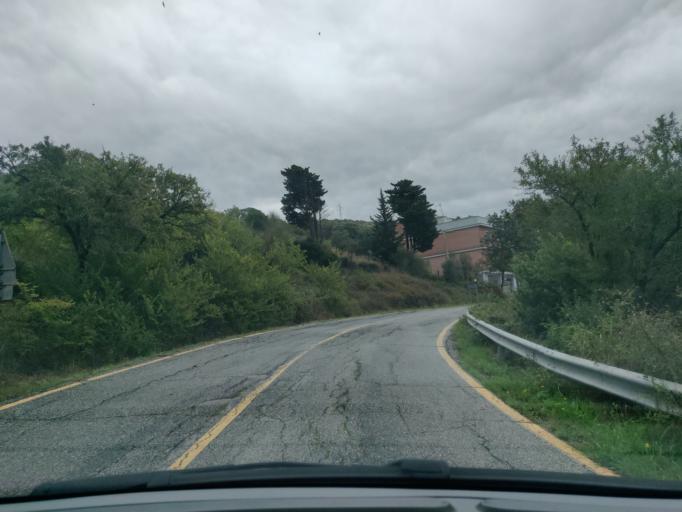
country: IT
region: Latium
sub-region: Citta metropolitana di Roma Capitale
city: Aurelia
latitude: 42.1341
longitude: 11.8397
